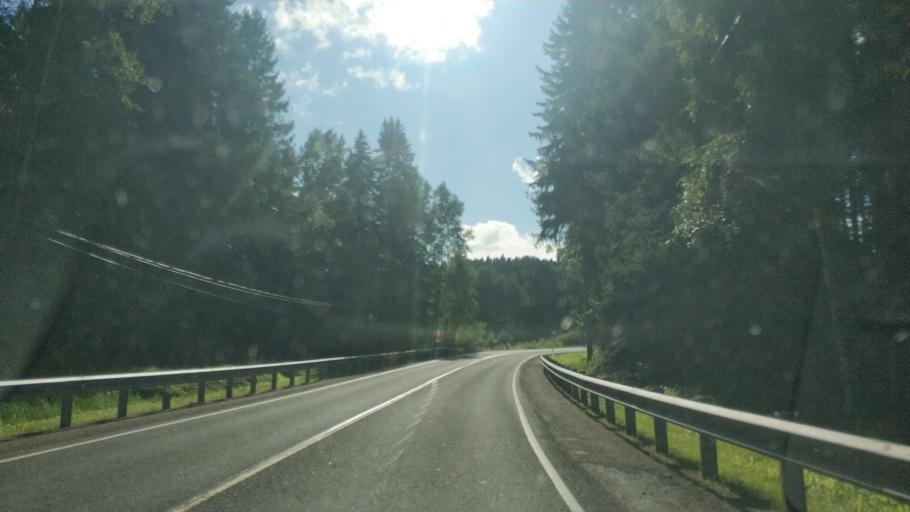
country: RU
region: Republic of Karelia
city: Sortavala
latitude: 61.6569
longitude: 30.6546
